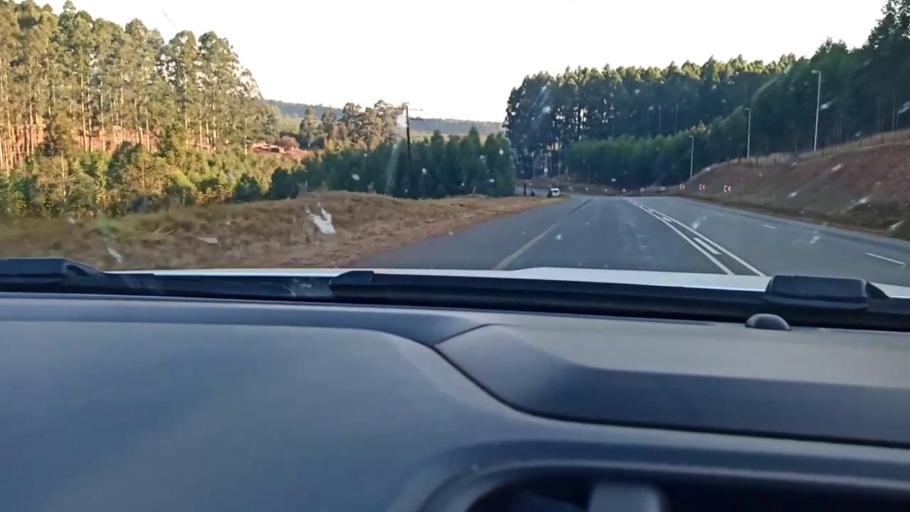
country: ZA
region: Limpopo
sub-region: Mopani District Municipality
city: Duiwelskloof
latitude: -23.7066
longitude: 30.1315
